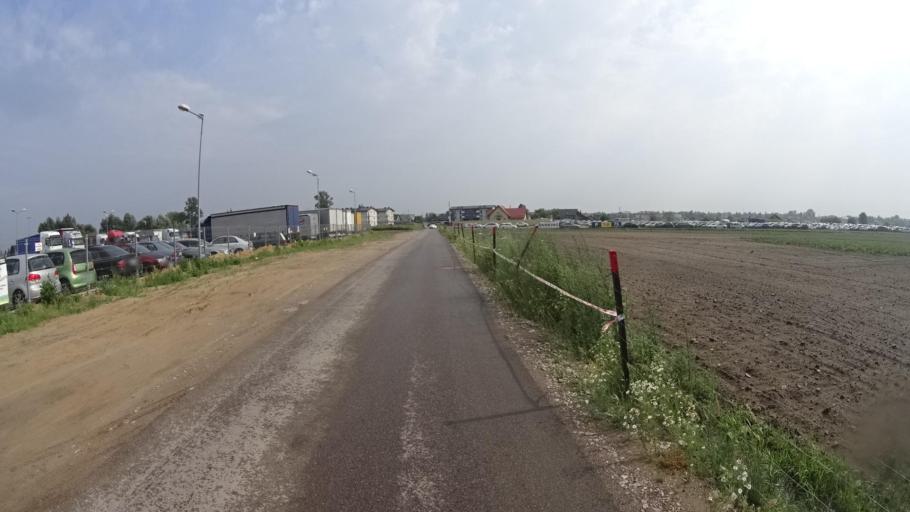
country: PL
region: Masovian Voivodeship
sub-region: Powiat pruszkowski
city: Nowe Grocholice
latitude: 52.1689
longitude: 20.9195
